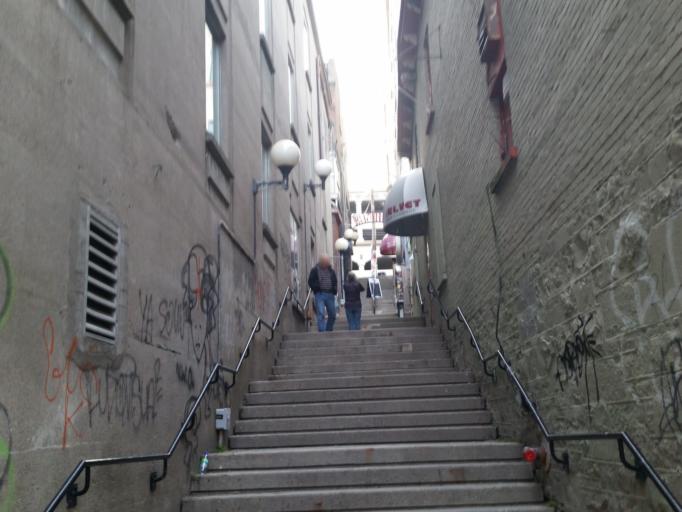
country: CA
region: Newfoundland and Labrador
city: St. John's
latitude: 47.5639
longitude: -52.7074
